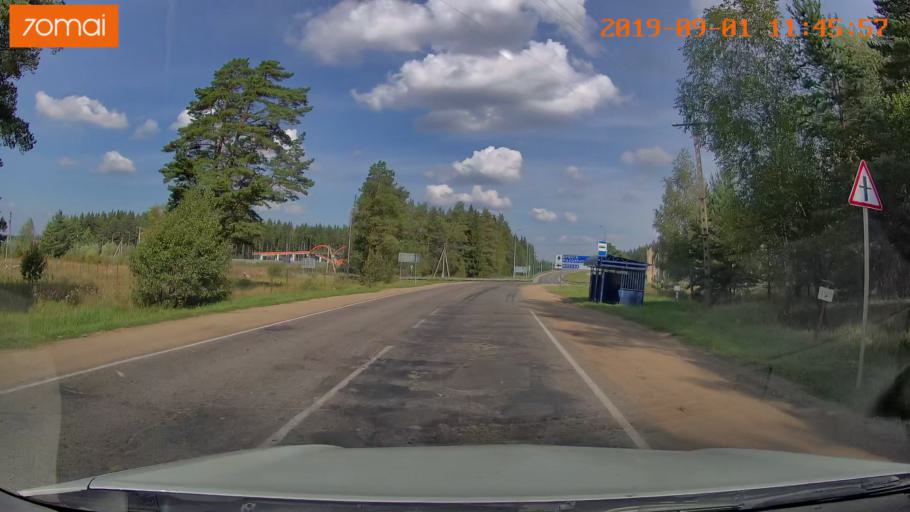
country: RU
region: Kaluga
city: Maloyaroslavets
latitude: 54.9216
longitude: 36.4049
